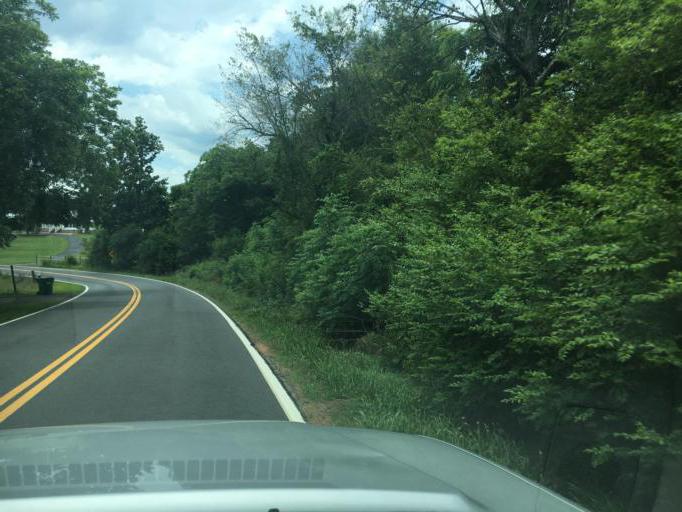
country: US
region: South Carolina
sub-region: Spartanburg County
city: Duncan
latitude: 34.8767
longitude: -82.1862
